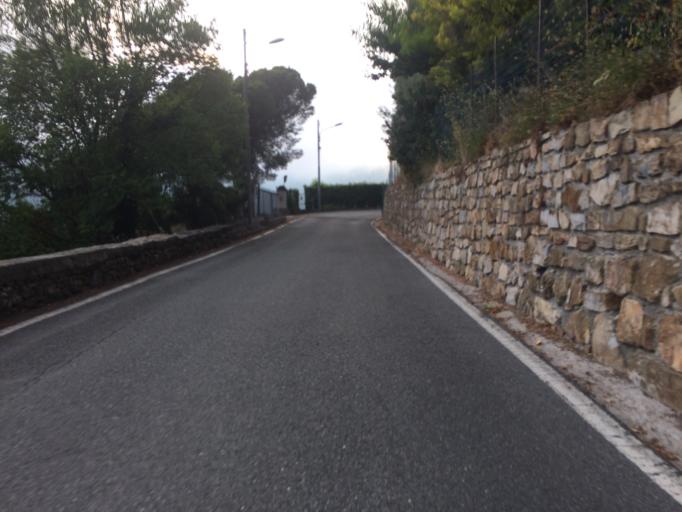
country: IT
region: Liguria
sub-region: Provincia di Imperia
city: San Remo
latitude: 43.8451
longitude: 7.7402
